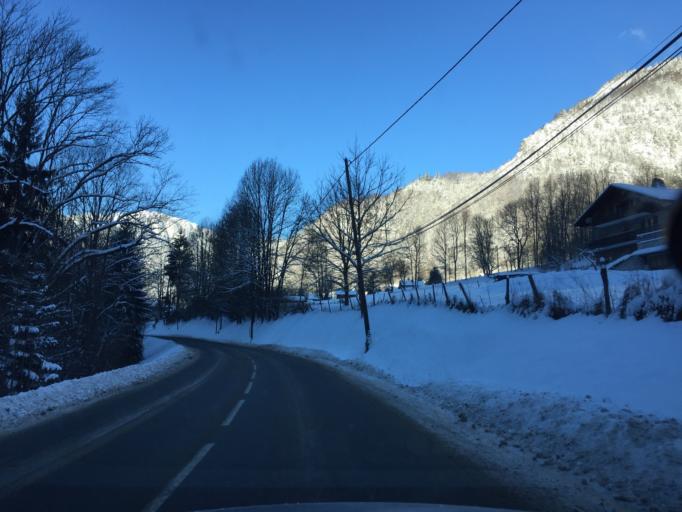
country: FR
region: Rhone-Alpes
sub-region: Departement de la Haute-Savoie
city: Abondance
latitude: 46.2833
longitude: 6.7037
